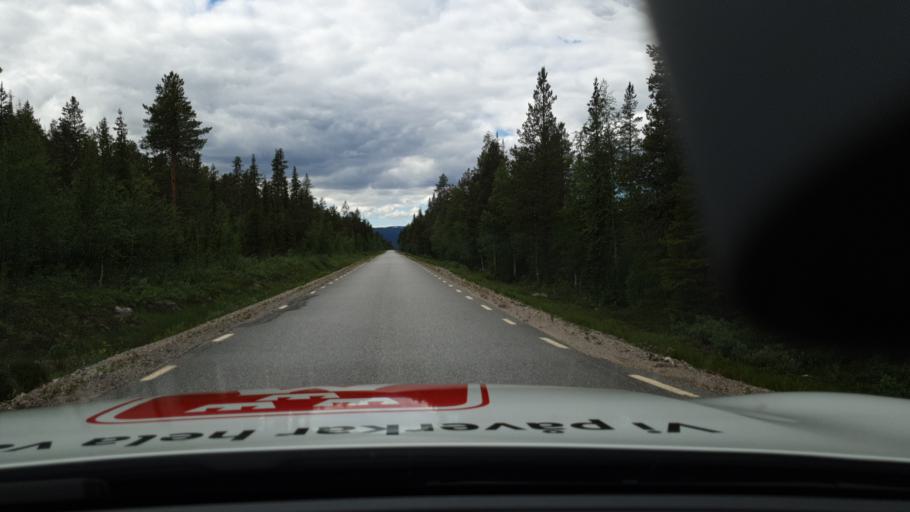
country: SE
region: Norrbotten
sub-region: Arjeplogs Kommun
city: Arjeplog
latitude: 66.8953
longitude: 17.9618
